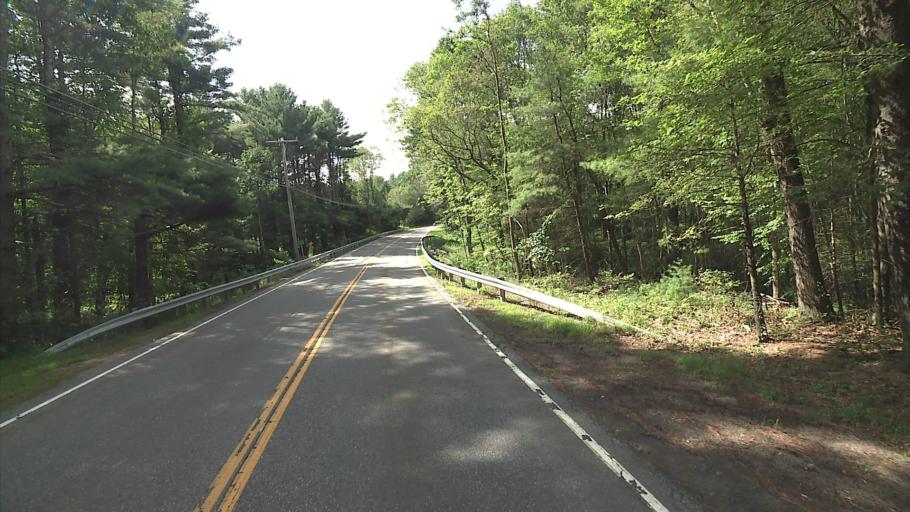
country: US
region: Massachusetts
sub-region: Hampden County
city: Holland
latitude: 42.0165
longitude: -72.1455
